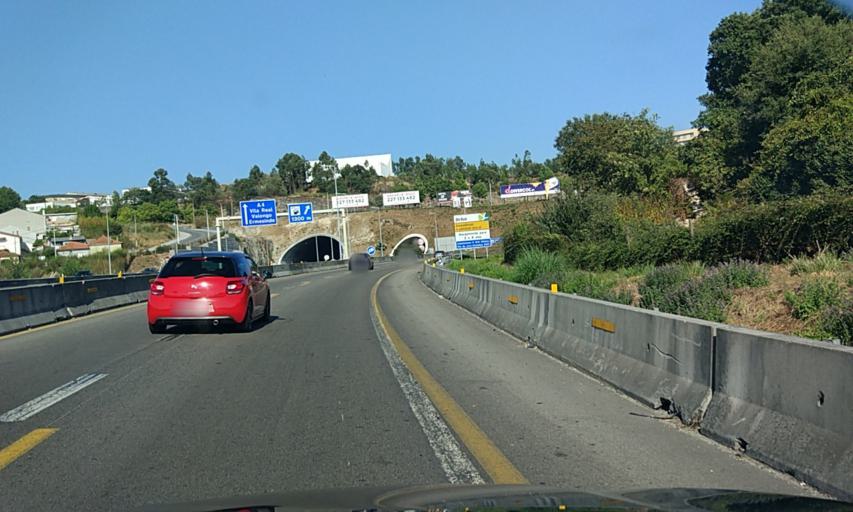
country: PT
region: Porto
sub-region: Maia
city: Pedroucos
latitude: 41.1982
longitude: -8.5811
